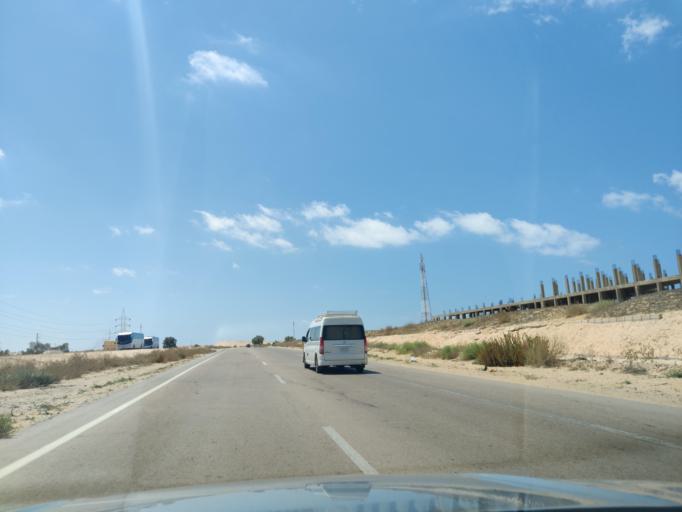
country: EG
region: Muhafazat Matruh
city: Al `Alamayn
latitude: 31.0609
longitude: 28.2035
